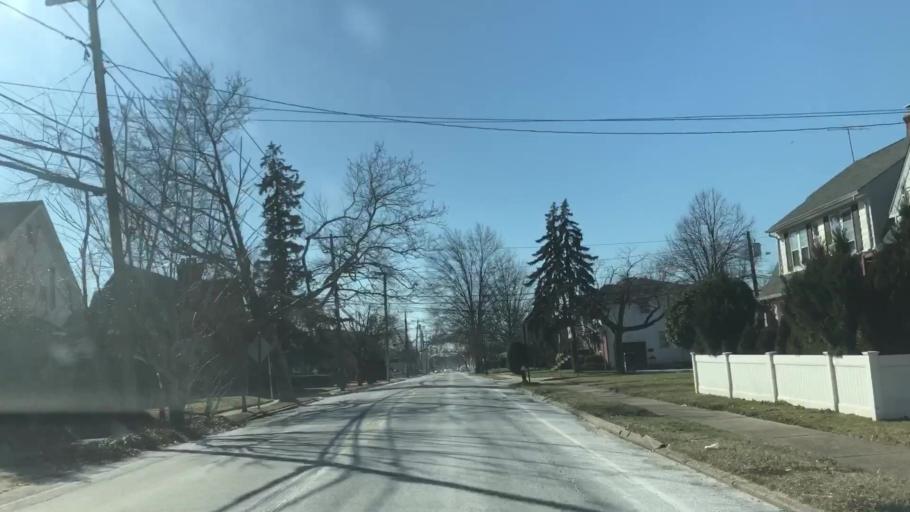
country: US
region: New York
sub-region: Nassau County
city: Valley Stream
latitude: 40.6676
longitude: -73.6985
